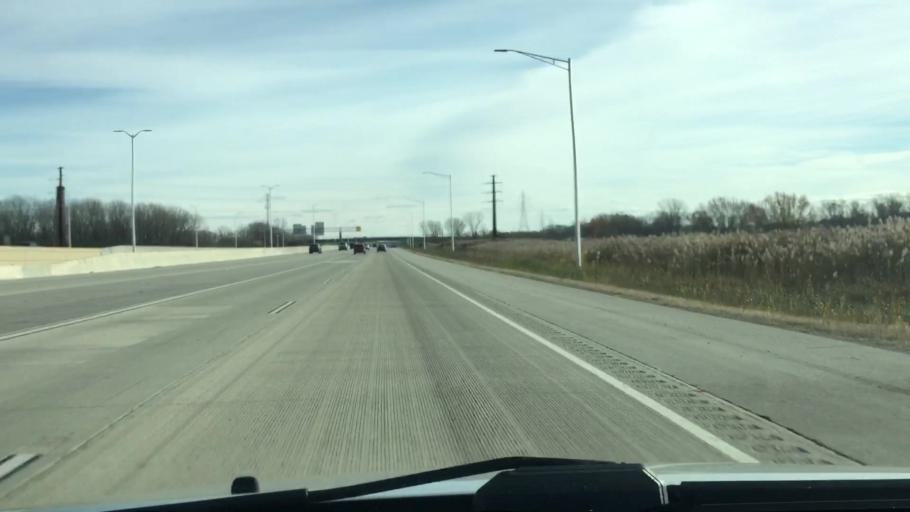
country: US
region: Wisconsin
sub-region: Brown County
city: Howard
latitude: 44.5562
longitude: -88.0480
